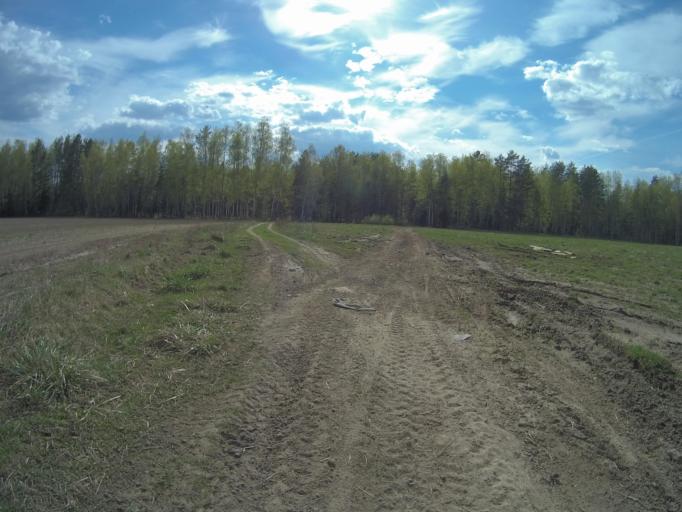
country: RU
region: Vladimir
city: Kommunar
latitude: 56.0414
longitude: 40.4686
